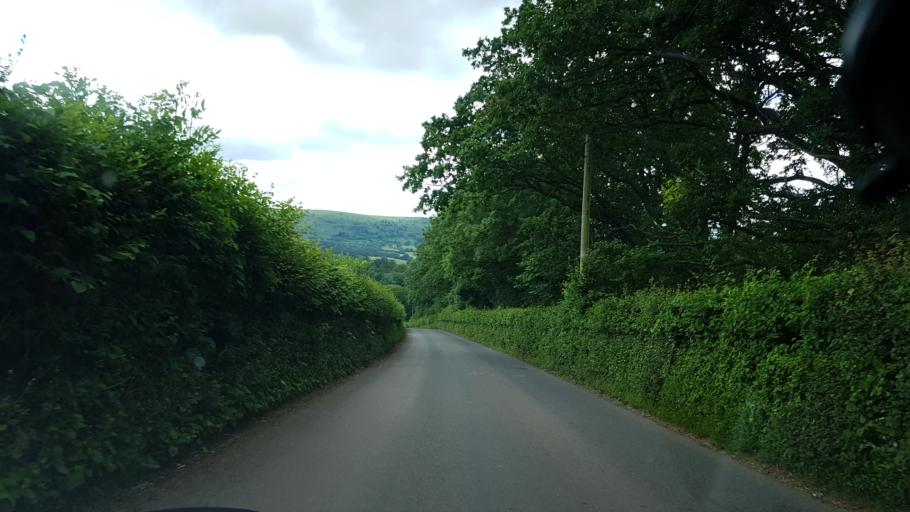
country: GB
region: England
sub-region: Herefordshire
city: Llancillo
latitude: 51.8812
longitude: -2.9665
